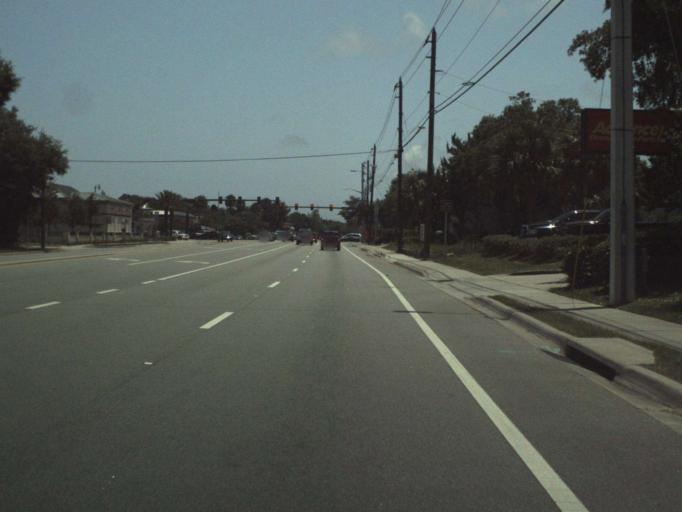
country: US
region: Florida
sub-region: Volusia County
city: Ormond Beach
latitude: 29.2846
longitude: -81.0630
